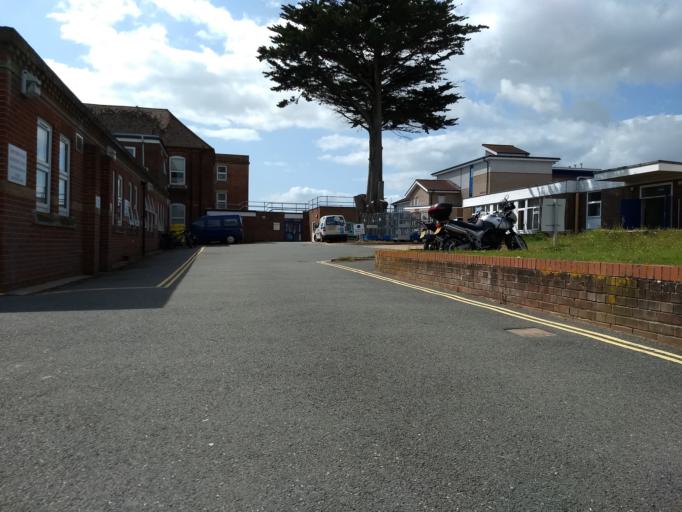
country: GB
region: England
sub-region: Isle of Wight
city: Newport
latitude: 50.7123
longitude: -1.3004
